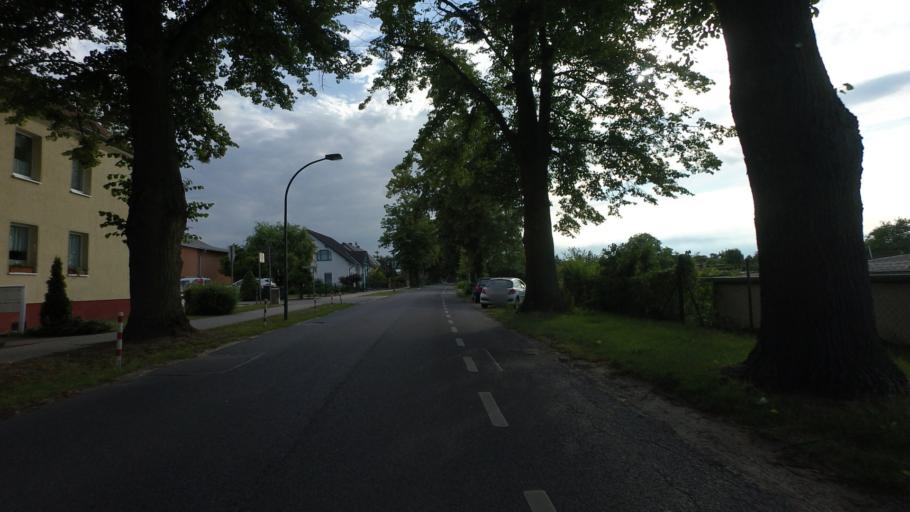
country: DE
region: Brandenburg
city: Nauen
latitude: 52.6032
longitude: 12.8664
